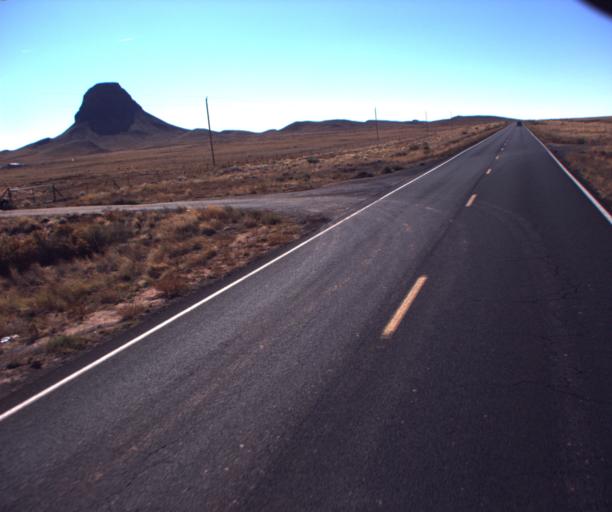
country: US
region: Arizona
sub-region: Navajo County
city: Dilkon
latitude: 35.3142
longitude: -110.4229
